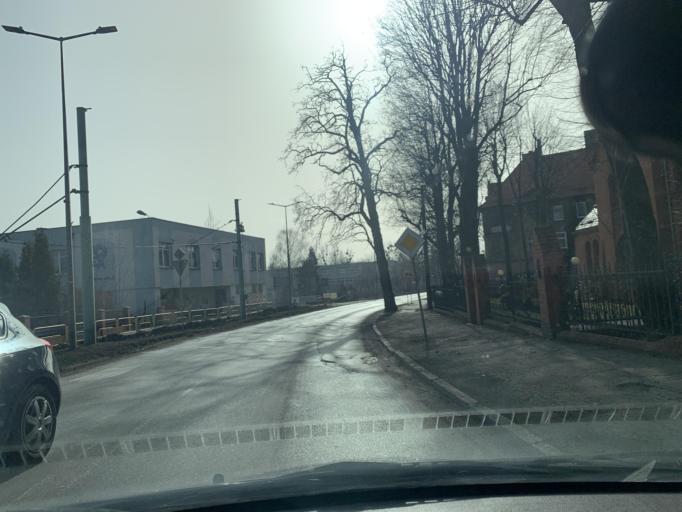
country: PL
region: Silesian Voivodeship
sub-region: Bytom
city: Bytom
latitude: 50.3359
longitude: 18.8968
